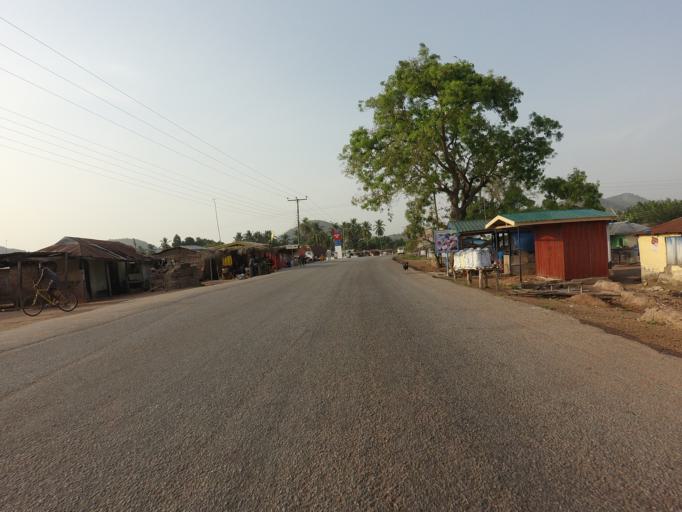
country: GH
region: Volta
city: Ho
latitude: 6.4081
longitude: 0.1730
